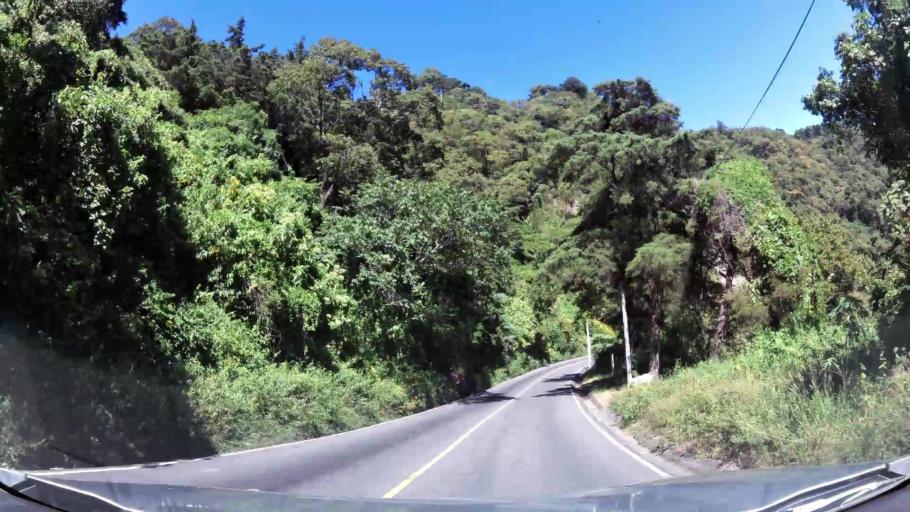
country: GT
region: Solola
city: Solola
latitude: 14.7544
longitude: -91.1695
